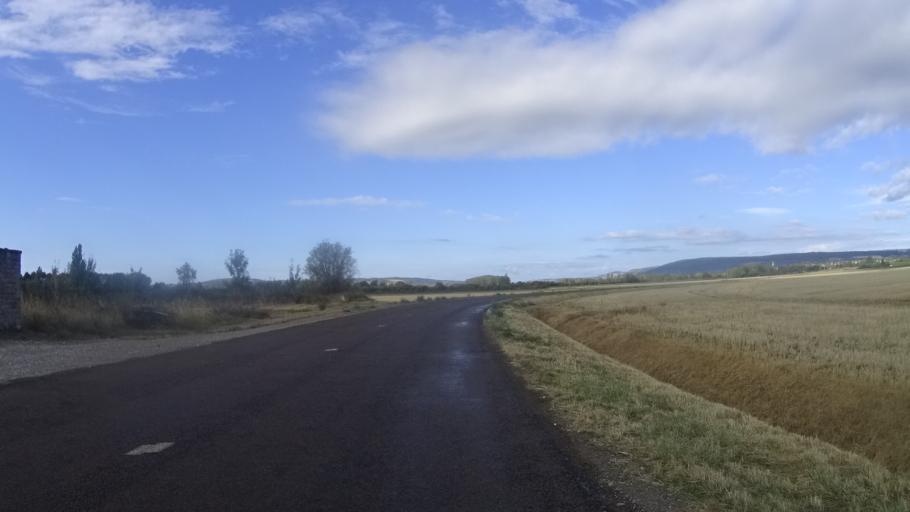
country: FR
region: Bourgogne
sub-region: Departement de la Cote-d'Or
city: Corpeau
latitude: 46.9267
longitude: 4.7794
